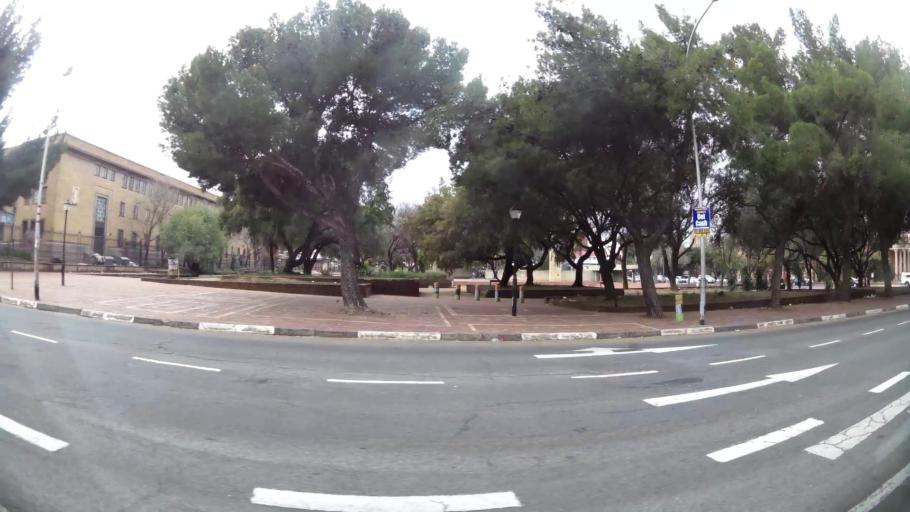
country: ZA
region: Orange Free State
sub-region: Mangaung Metropolitan Municipality
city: Bloemfontein
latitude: -29.1146
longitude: 26.2174
